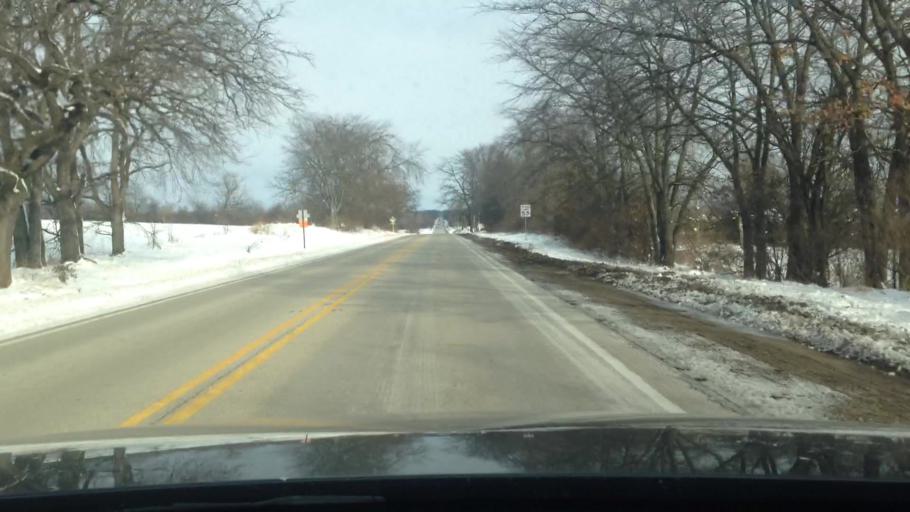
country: US
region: Illinois
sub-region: McHenry County
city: Woodstock
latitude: 42.3617
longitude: -88.4431
